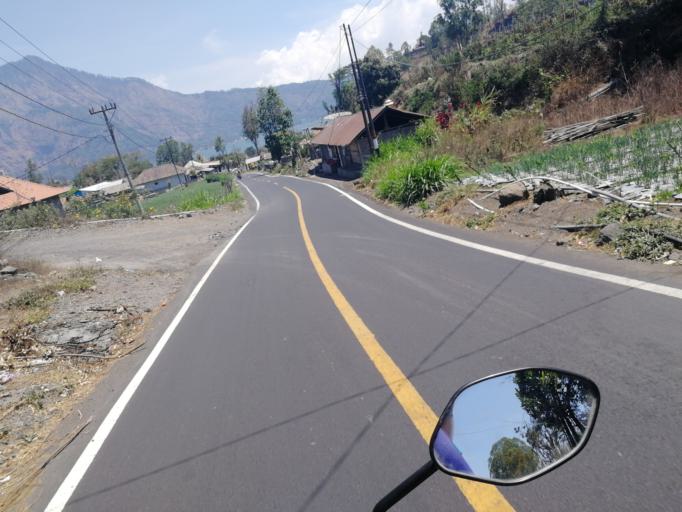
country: ID
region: Bali
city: Banjar Trunyan
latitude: -8.2352
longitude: 115.4057
